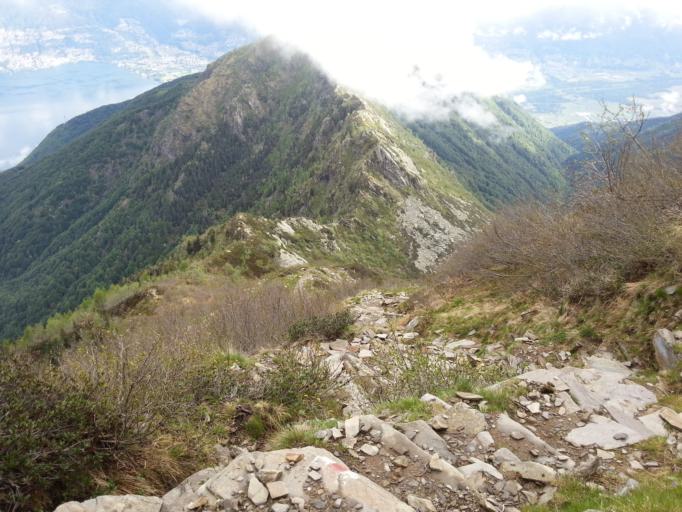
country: CH
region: Ticino
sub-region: Locarno District
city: Magadino
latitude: 46.1042
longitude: 8.8653
